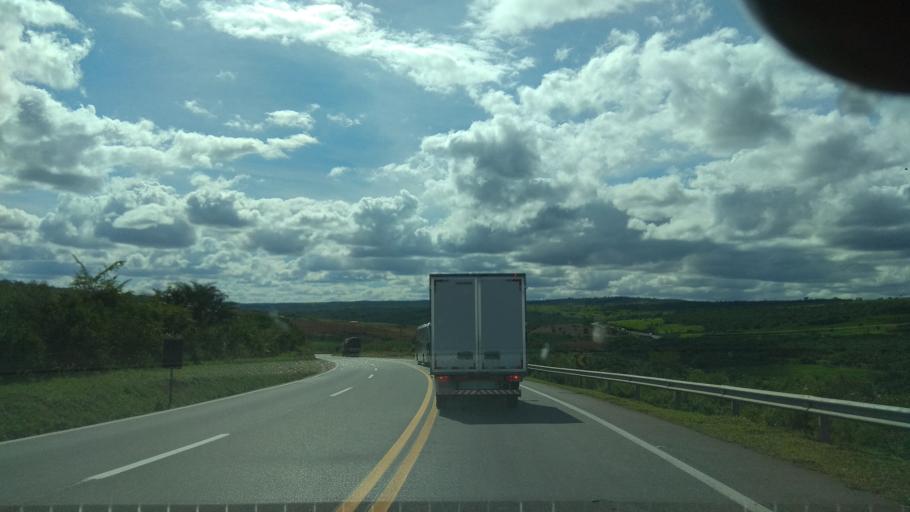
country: BR
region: Bahia
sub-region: Santa Ines
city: Santa Ines
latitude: -13.1671
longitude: -39.9977
